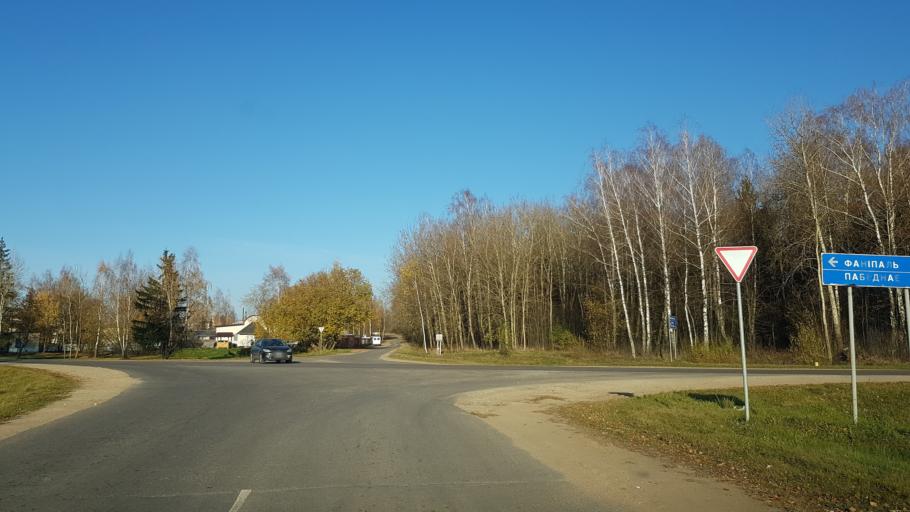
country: BY
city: Fanipol
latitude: 53.7303
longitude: 27.3323
